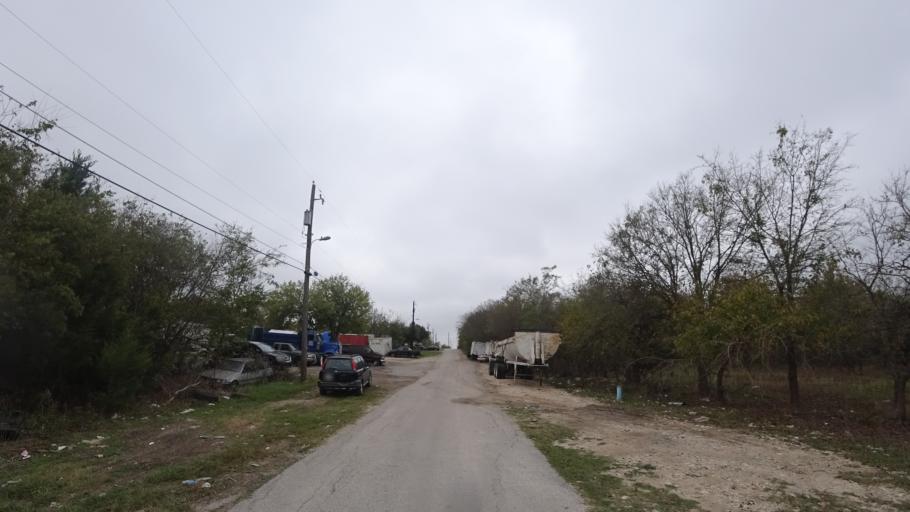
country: US
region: Texas
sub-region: Travis County
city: Pflugerville
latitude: 30.3764
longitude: -97.6223
